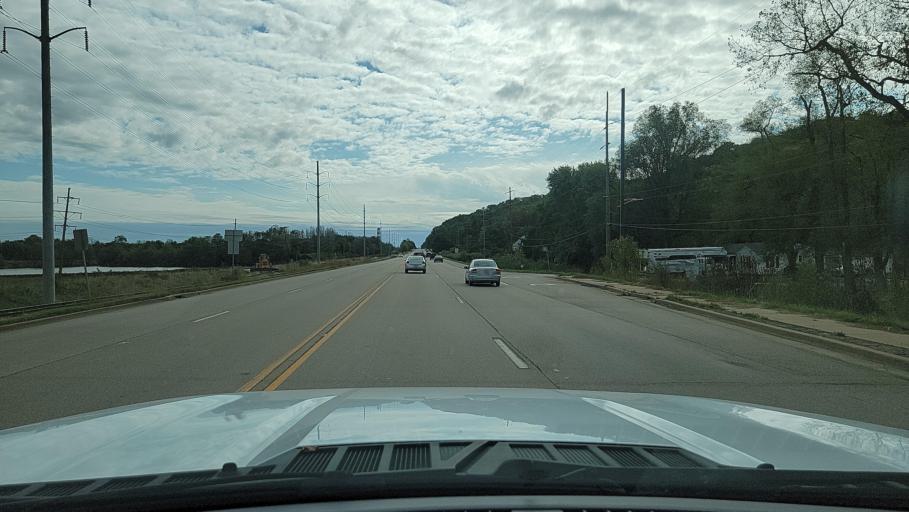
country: US
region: Illinois
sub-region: Peoria County
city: Bartonville
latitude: 40.6298
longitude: -89.6533
